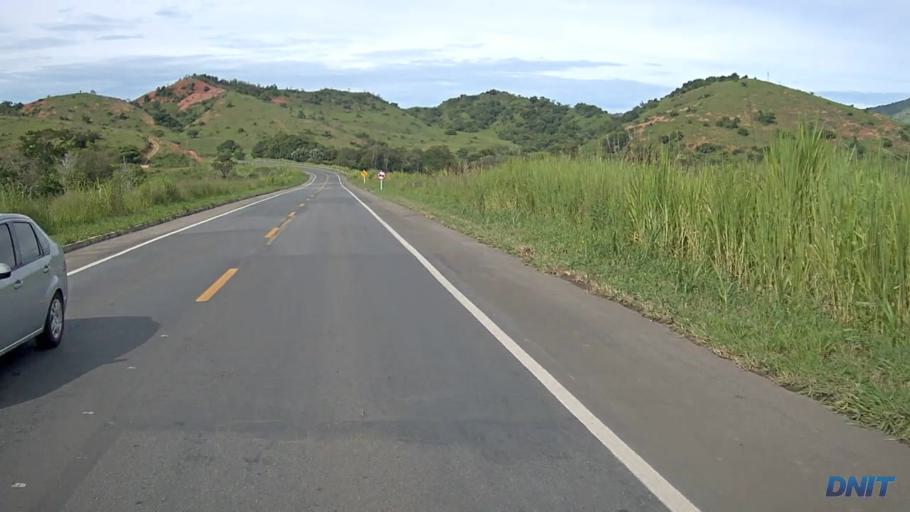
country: BR
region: Minas Gerais
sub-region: Belo Oriente
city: Belo Oriente
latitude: -19.2196
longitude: -42.3098
